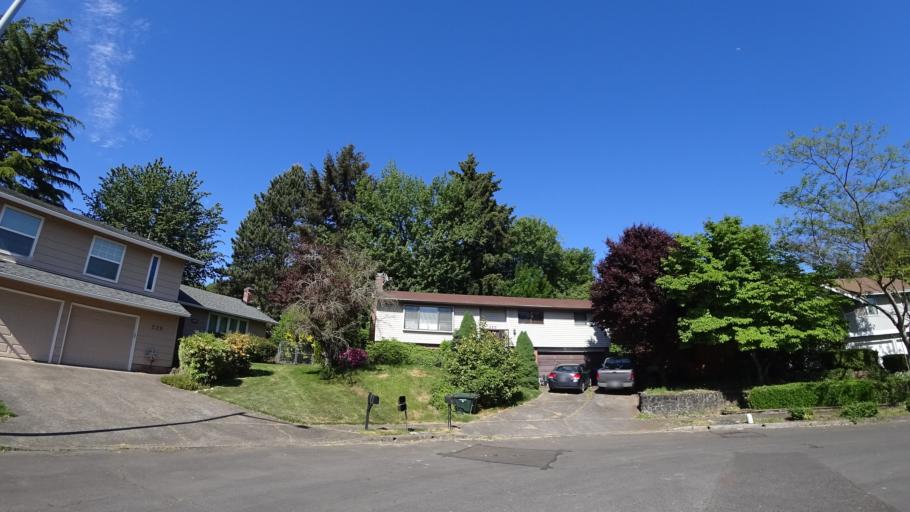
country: US
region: Oregon
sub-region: Multnomah County
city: Gresham
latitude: 45.4987
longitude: -122.4719
